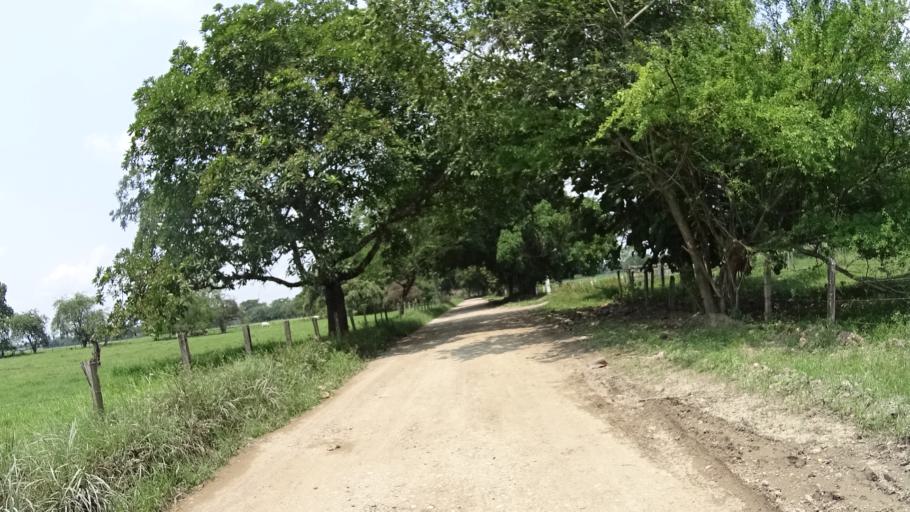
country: CO
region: Cundinamarca
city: Puerto Salgar
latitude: 5.5249
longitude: -74.6865
